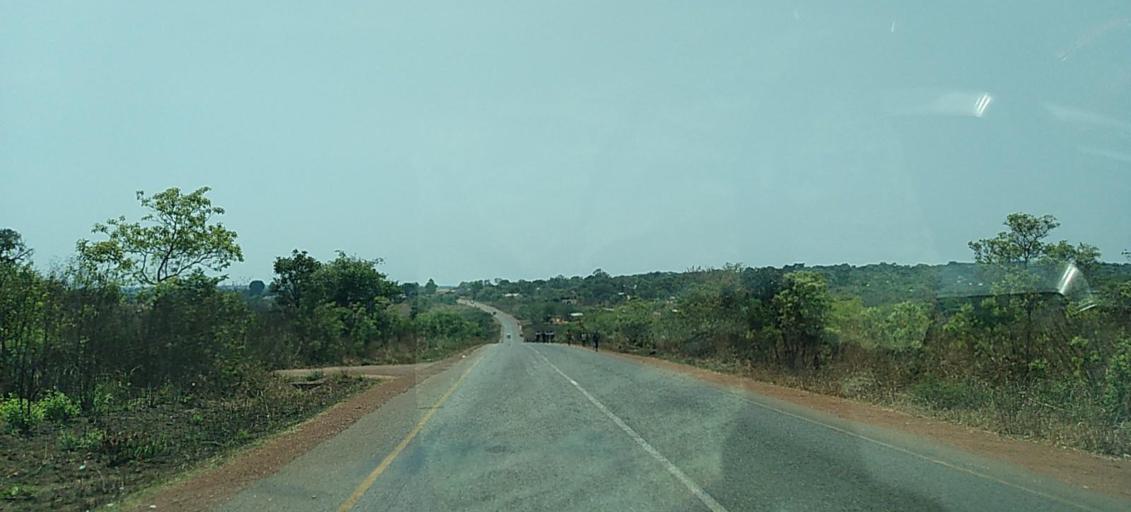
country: ZM
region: North-Western
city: Solwezi
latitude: -12.3950
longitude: 26.2297
